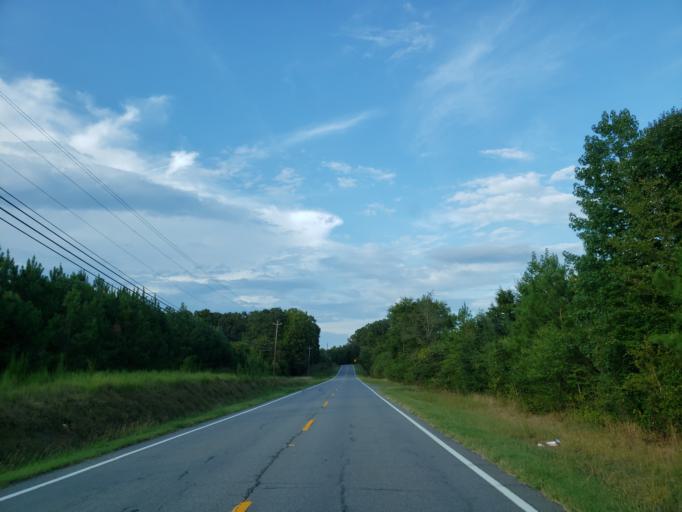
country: US
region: Georgia
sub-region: Bartow County
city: Euharlee
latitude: 34.2411
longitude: -84.9223
